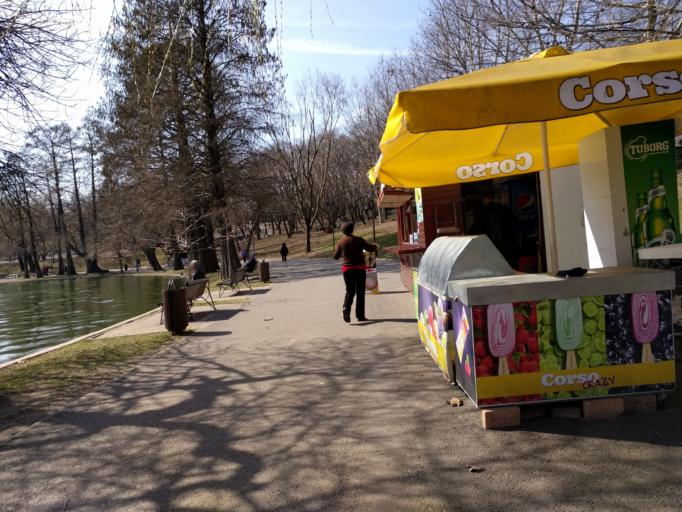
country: RO
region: Ilfov
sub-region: Comuna Fundeni-Dobroesti
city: Fundeni
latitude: 44.4279
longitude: 26.1557
